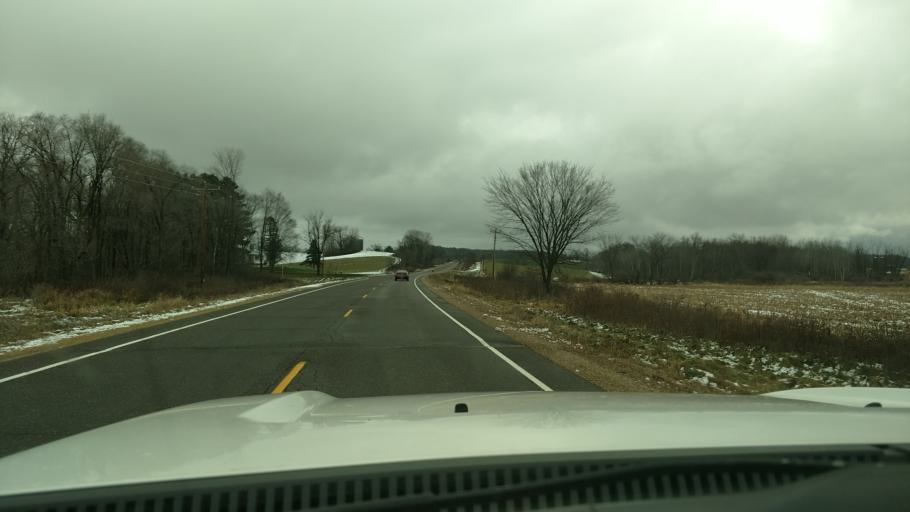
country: US
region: Wisconsin
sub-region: Dunn County
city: Boyceville
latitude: 45.1397
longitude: -91.9647
